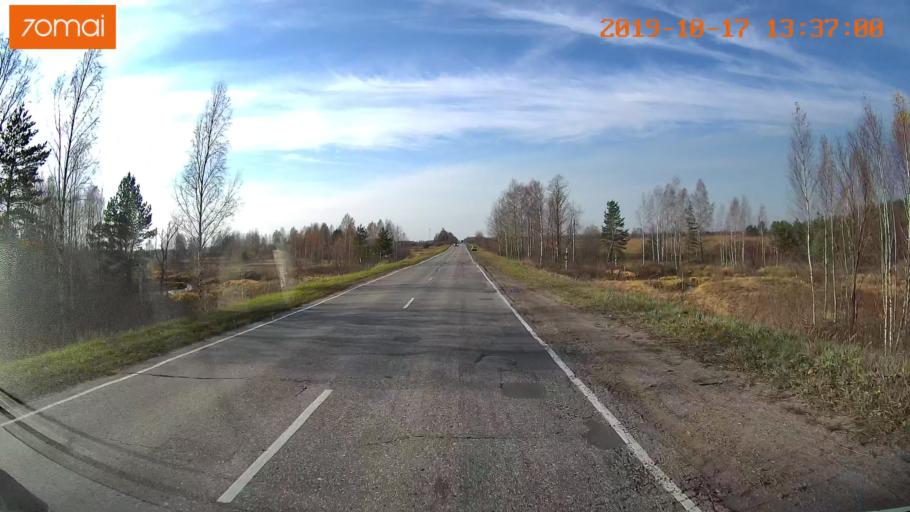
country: RU
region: Rjazan
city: Tuma
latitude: 55.1406
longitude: 40.6493
